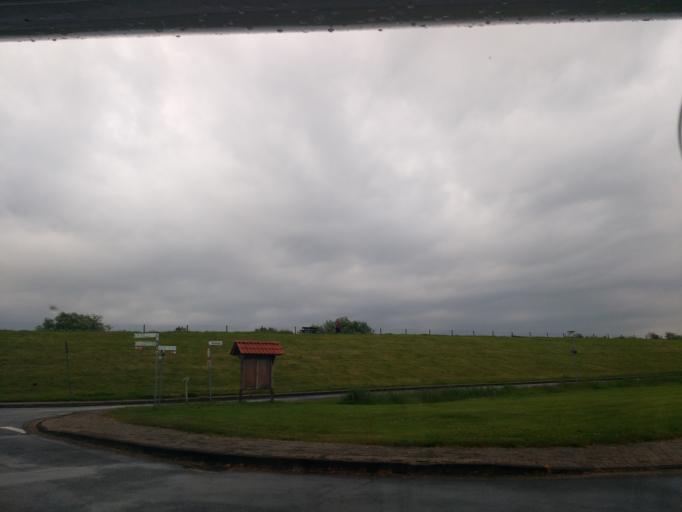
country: DE
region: Lower Saxony
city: Schillig
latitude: 53.6984
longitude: 8.0181
